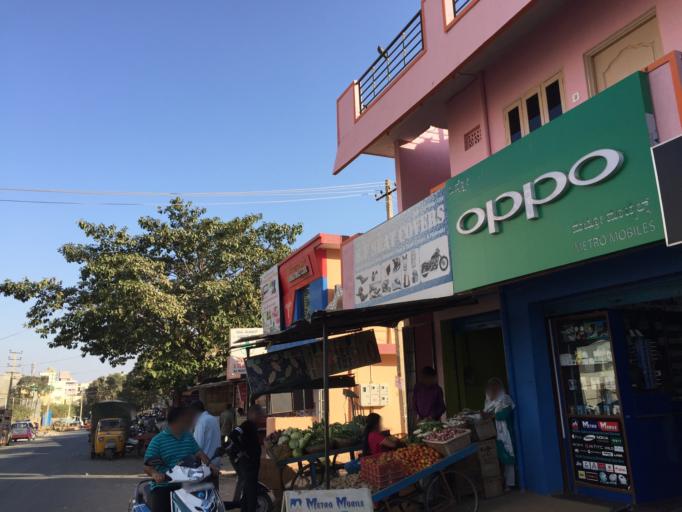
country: IN
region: Karnataka
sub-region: Bangalore Urban
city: Yelahanka
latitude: 13.0572
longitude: 77.6278
